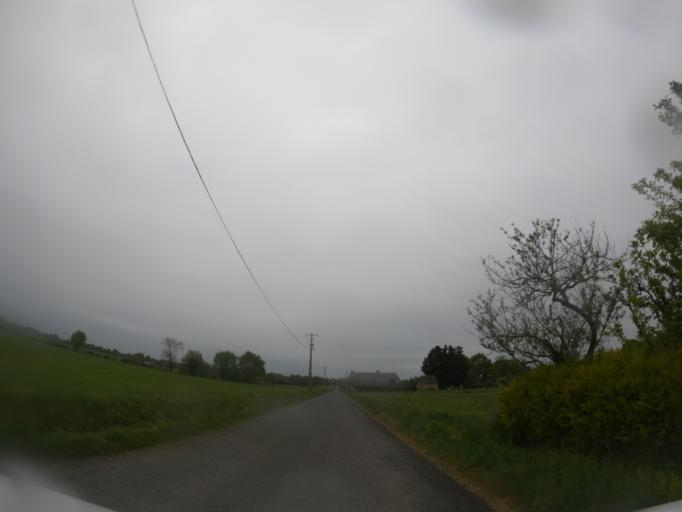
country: FR
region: Pays de la Loire
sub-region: Departement de la Mayenne
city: Ballots
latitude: 47.9565
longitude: -1.1284
